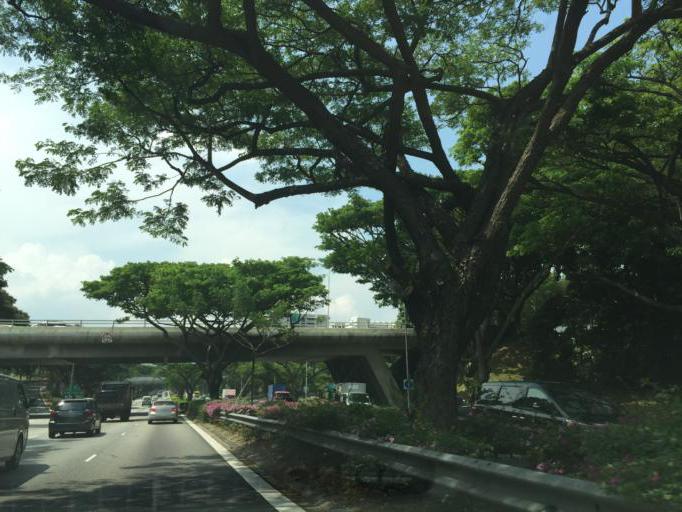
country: SG
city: Singapore
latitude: 1.3322
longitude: 103.9190
